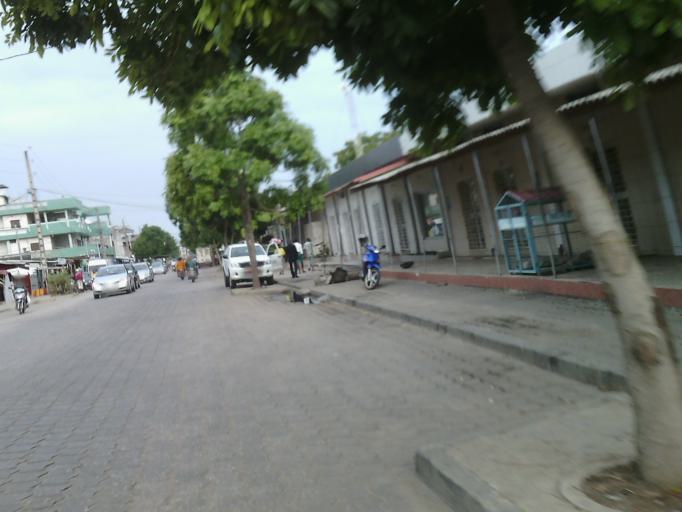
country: BJ
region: Littoral
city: Cotonou
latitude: 6.3886
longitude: 2.3782
